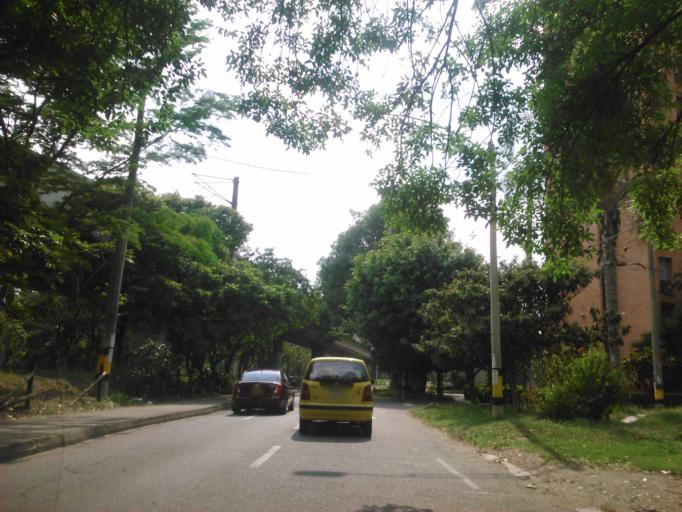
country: CO
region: Antioquia
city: Medellin
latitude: 6.2534
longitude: -75.5841
